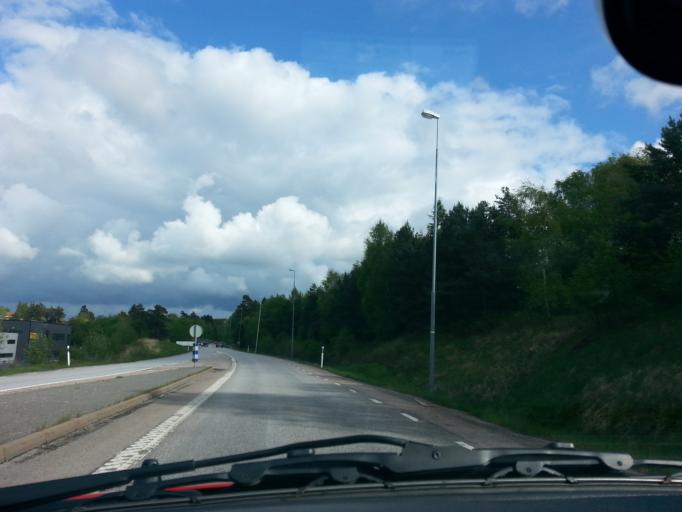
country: SE
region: Vaestra Goetaland
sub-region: Partille Kommun
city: Furulund
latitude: 57.7231
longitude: 12.1307
